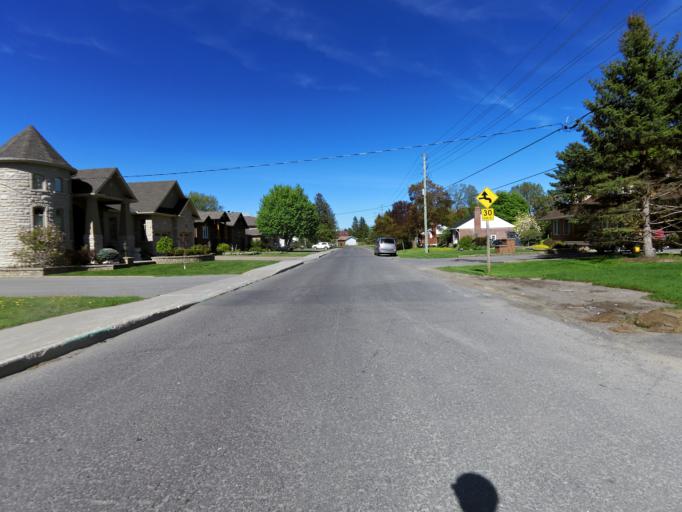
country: CA
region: Ontario
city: Bells Corners
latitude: 45.3412
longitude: -75.7492
